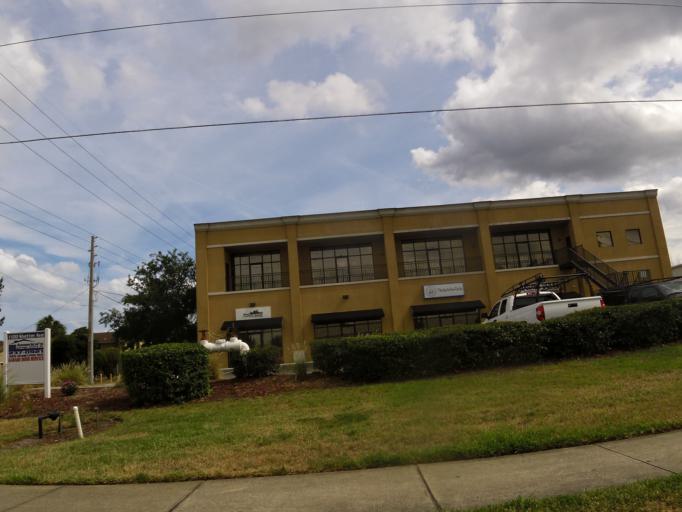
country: US
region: Florida
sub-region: Duval County
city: Jacksonville Beach
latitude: 30.2869
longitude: -81.3997
